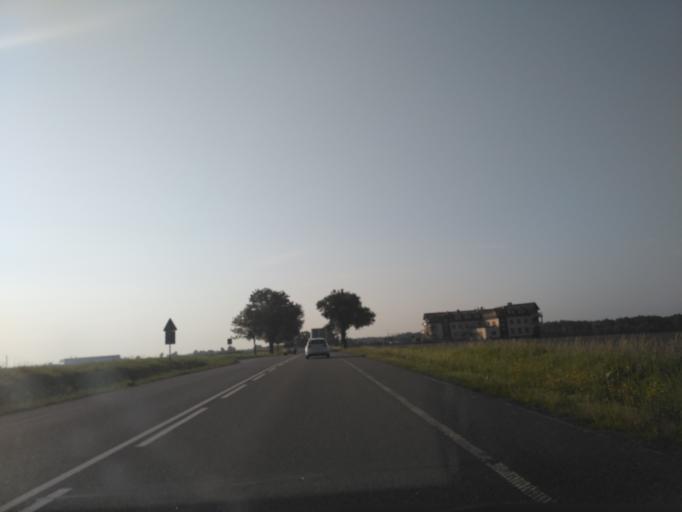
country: PL
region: Lublin Voivodeship
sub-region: Powiat janowski
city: Modliborzyce
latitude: 50.7291
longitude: 22.3616
